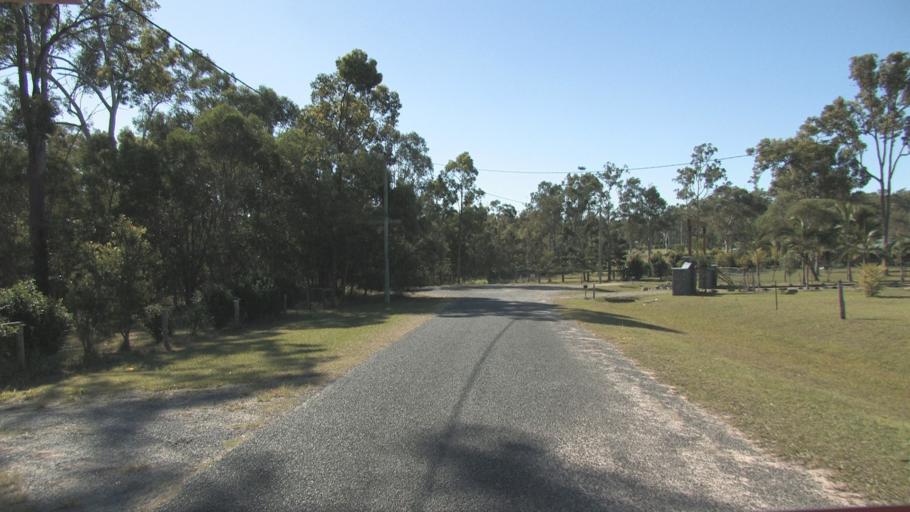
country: AU
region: Queensland
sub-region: Logan
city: Logan Reserve
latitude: -27.7258
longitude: 153.0673
